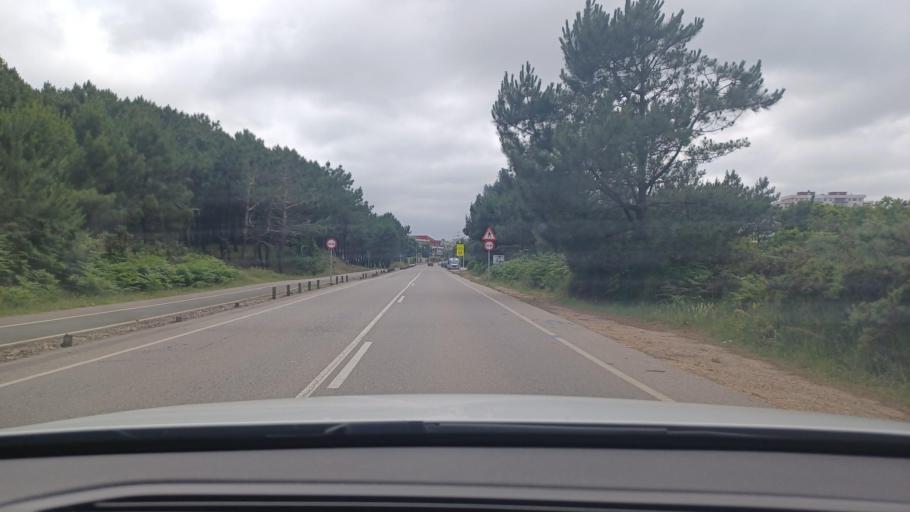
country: ES
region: Asturias
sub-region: Province of Asturias
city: Aviles
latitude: 43.5805
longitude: -5.9470
